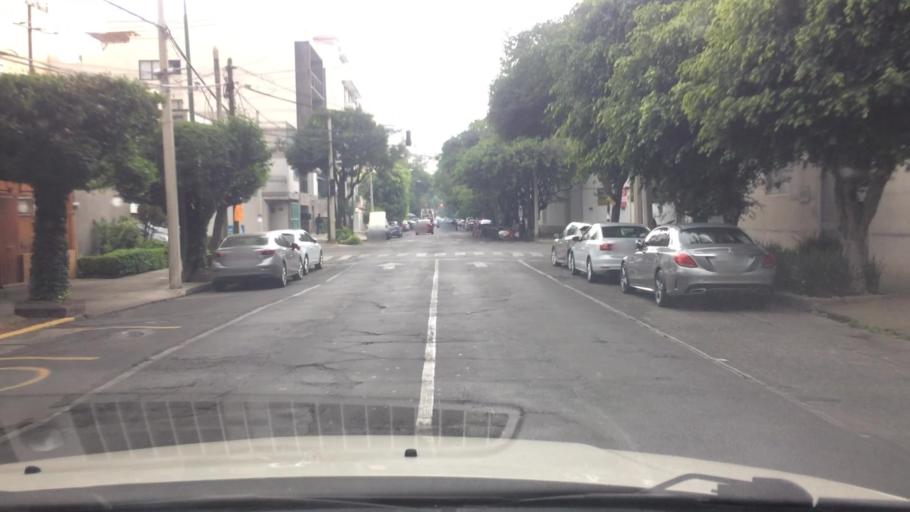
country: MX
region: Mexico City
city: Colonia del Valle
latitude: 19.3742
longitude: -99.1737
